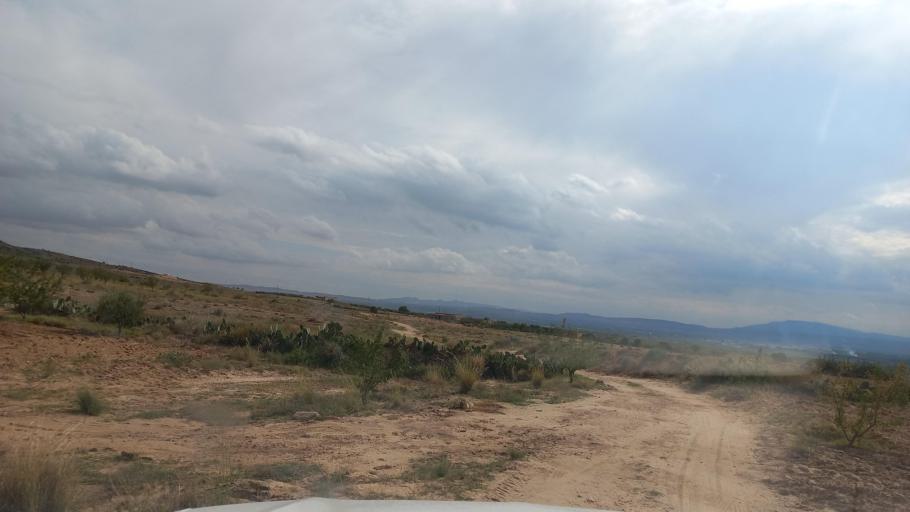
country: TN
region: Al Qasrayn
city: Sbiba
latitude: 35.3005
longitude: 9.1204
